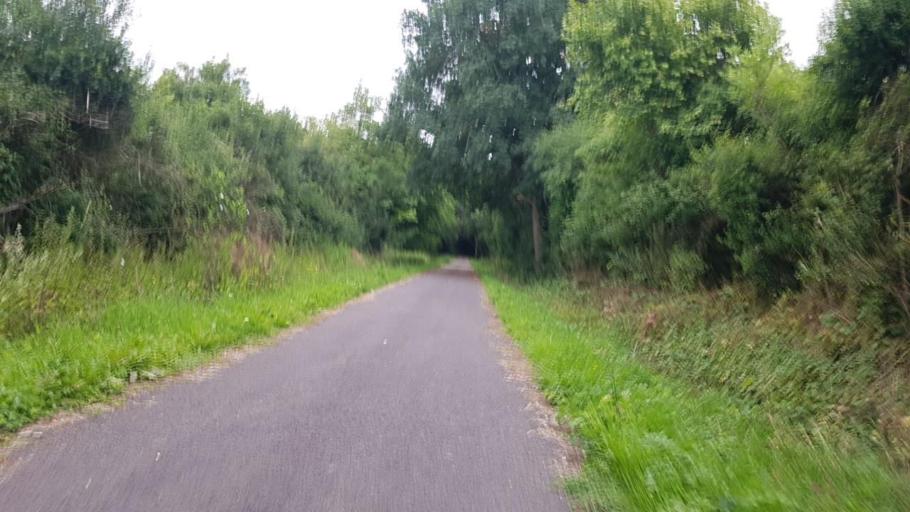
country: FR
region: Picardie
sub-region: Departement de l'Aisne
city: Buironfosse
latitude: 49.9017
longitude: 3.8711
